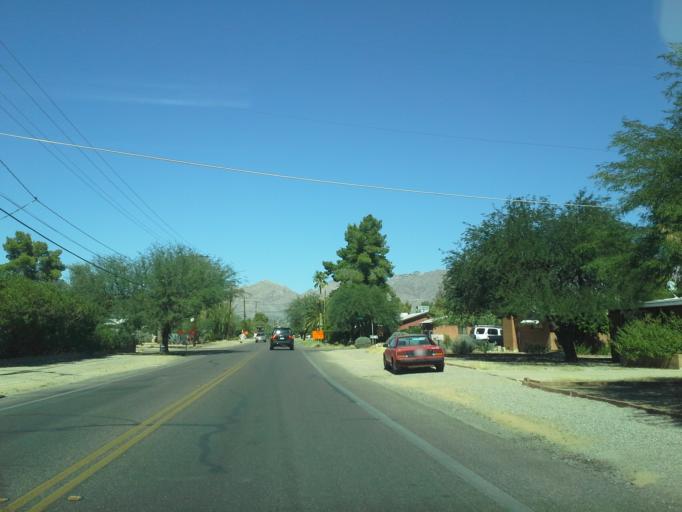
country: US
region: Arizona
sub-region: Pima County
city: Catalina Foothills
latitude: 32.2662
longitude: -110.9352
